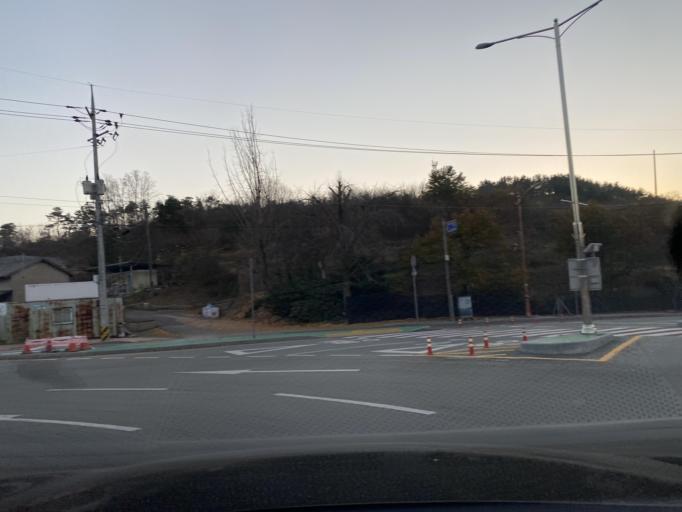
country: KR
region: Chungcheongnam-do
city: Yesan
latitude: 36.6868
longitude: 126.8429
